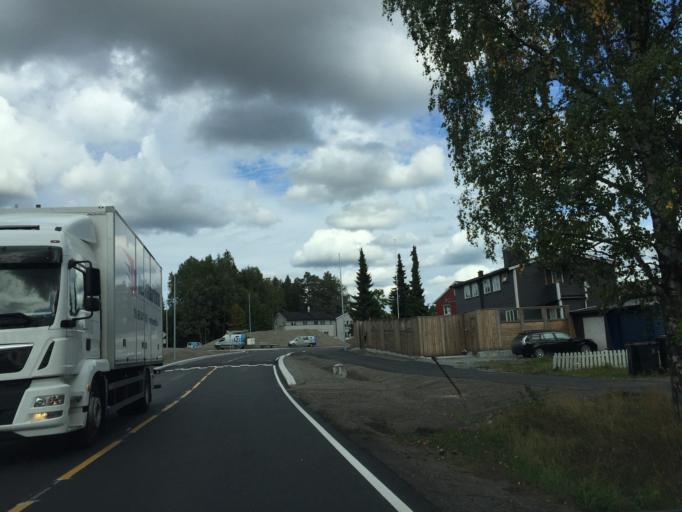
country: NO
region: Ostfold
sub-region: Hobol
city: Elvestad
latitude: 59.6220
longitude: 10.9483
